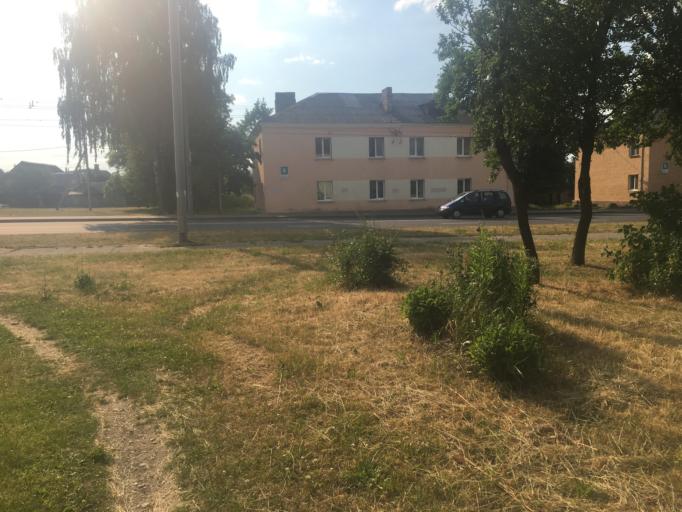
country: BY
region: Grodnenskaya
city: Hrodna
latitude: 53.6648
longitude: 23.8011
